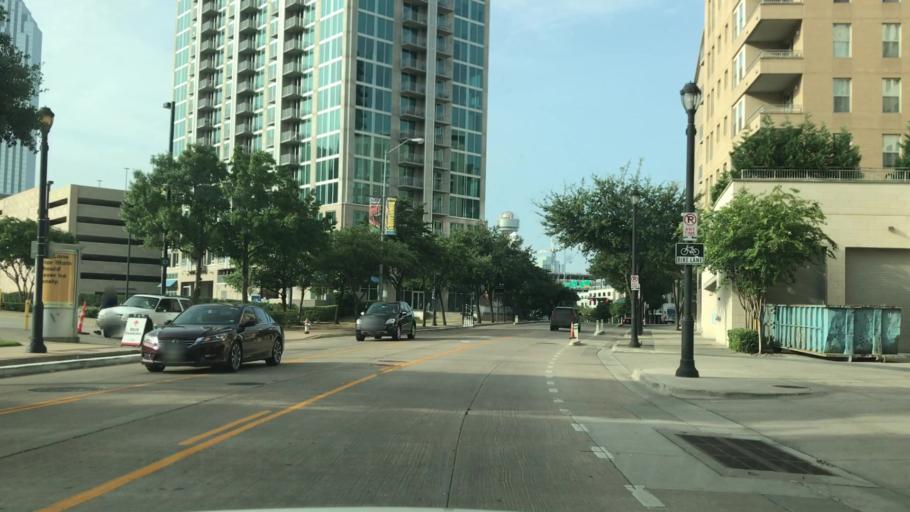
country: US
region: Texas
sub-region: Dallas County
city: Dallas
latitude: 32.7870
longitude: -96.8087
